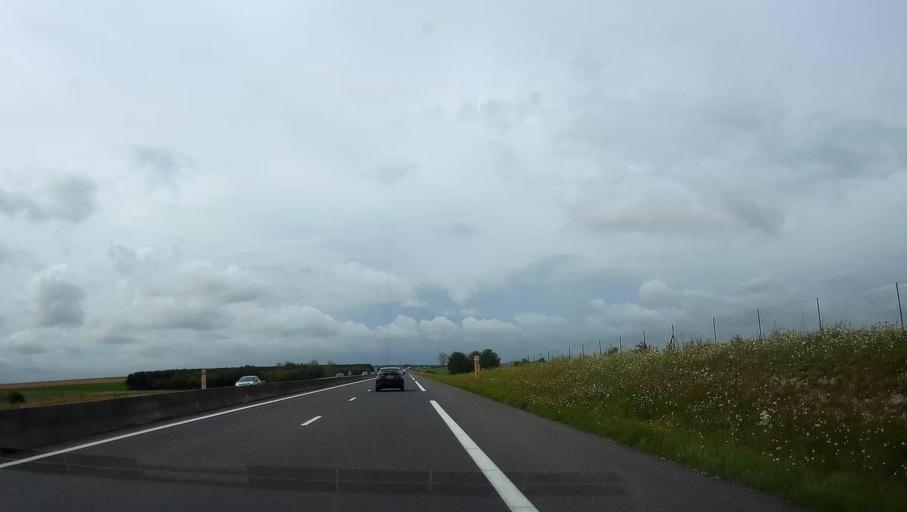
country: FR
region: Champagne-Ardenne
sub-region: Departement de l'Aube
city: Mailly-le-Camp
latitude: 48.7873
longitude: 4.2664
